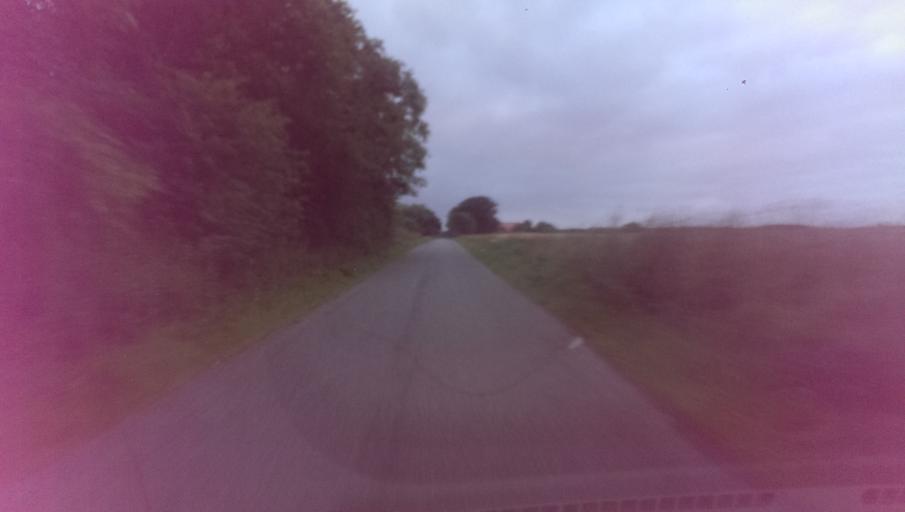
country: DK
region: South Denmark
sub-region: Esbjerg Kommune
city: Tjaereborg
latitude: 55.4788
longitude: 8.5204
